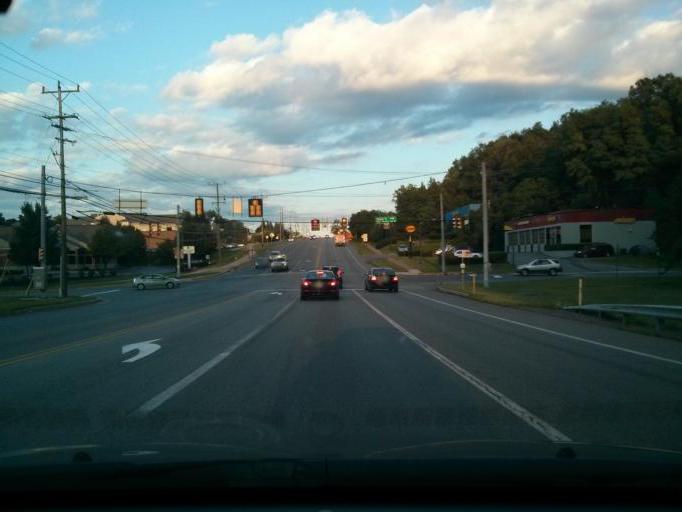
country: US
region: Pennsylvania
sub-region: Centre County
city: Park Forest Village
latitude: 40.8103
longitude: -77.9149
